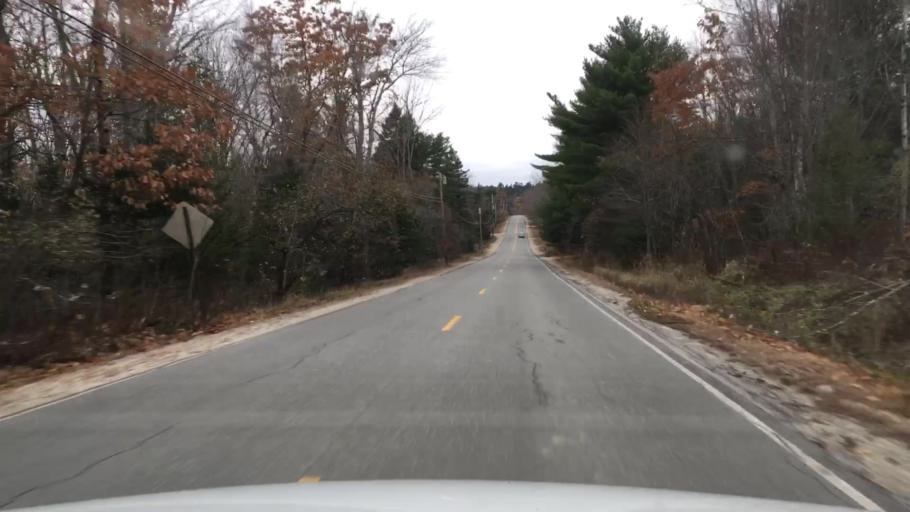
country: US
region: Maine
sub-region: Hancock County
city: Penobscot
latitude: 44.4182
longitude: -68.6139
